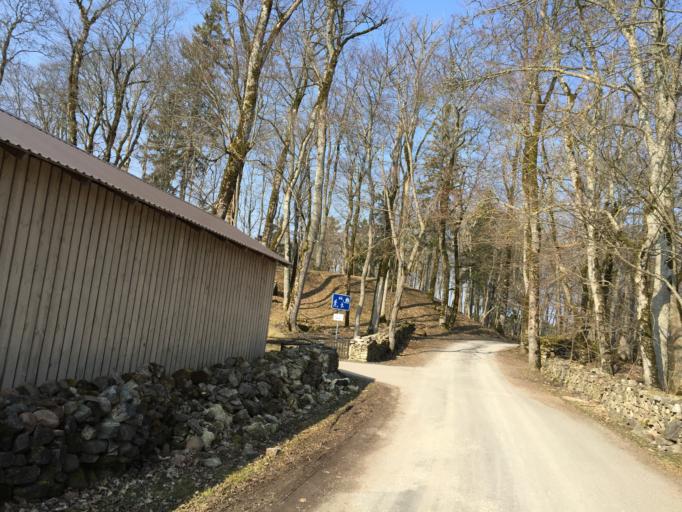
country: EE
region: Saare
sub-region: Kuressaare linn
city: Kuressaare
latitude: 58.3722
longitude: 22.6710
